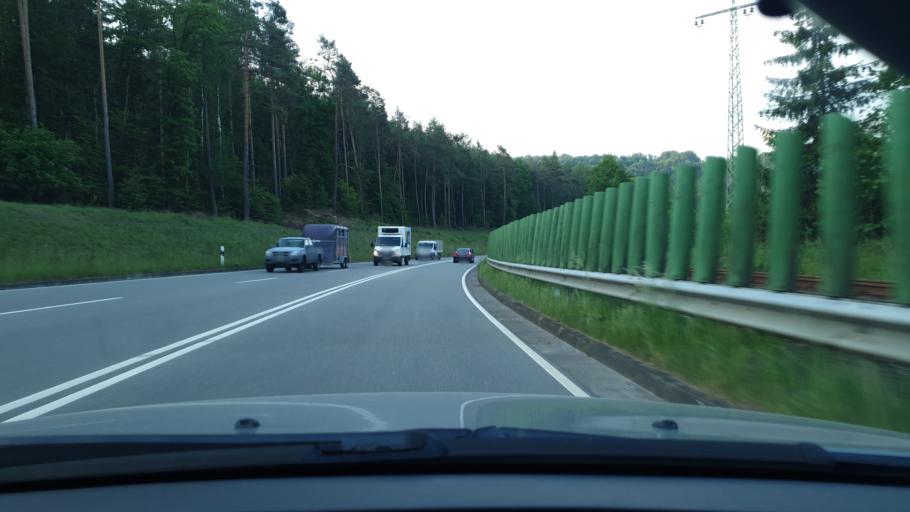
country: DE
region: Rheinland-Pfalz
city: Schopp
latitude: 49.3326
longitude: 7.6724
